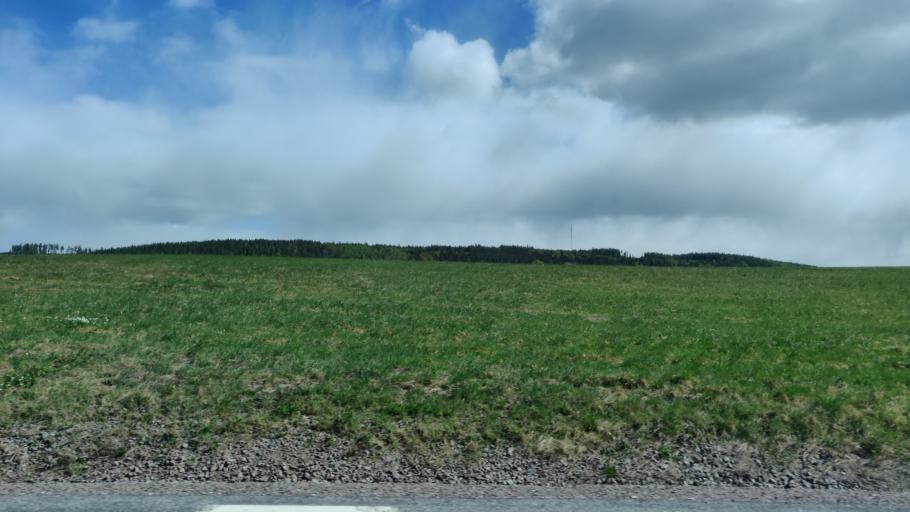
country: SE
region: Vaermland
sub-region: Hagfors Kommun
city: Hagfors
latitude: 59.9016
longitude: 13.6756
